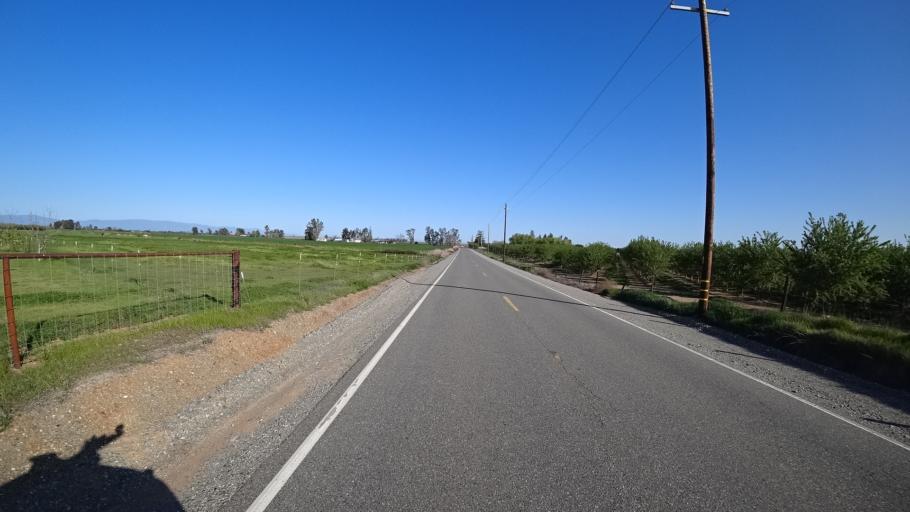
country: US
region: California
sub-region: Glenn County
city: Orland
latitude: 39.7639
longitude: -122.1075
